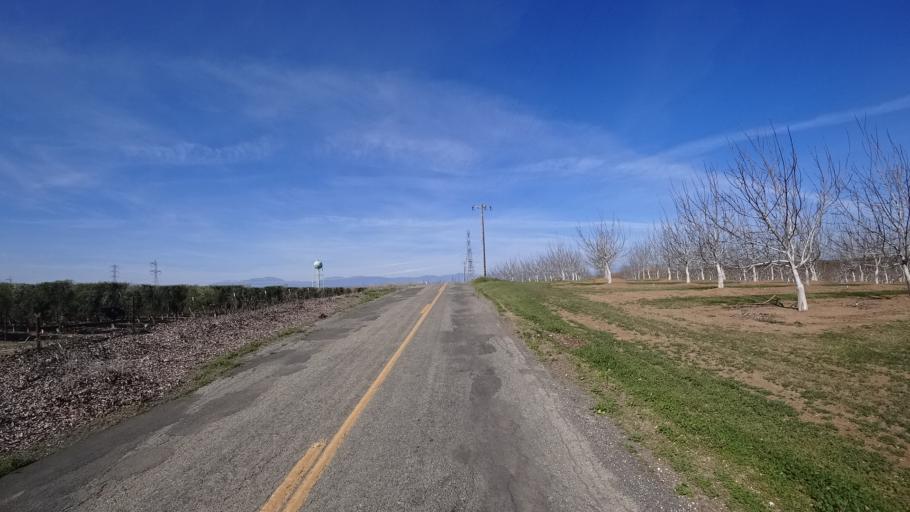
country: US
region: California
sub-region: Glenn County
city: Willows
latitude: 39.6117
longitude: -122.2699
